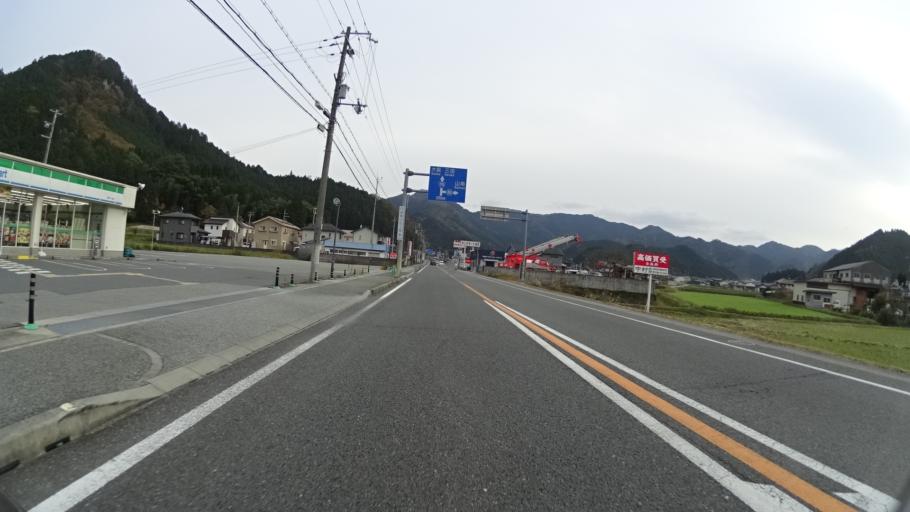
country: JP
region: Hyogo
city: Sasayama
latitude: 35.1215
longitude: 135.0862
